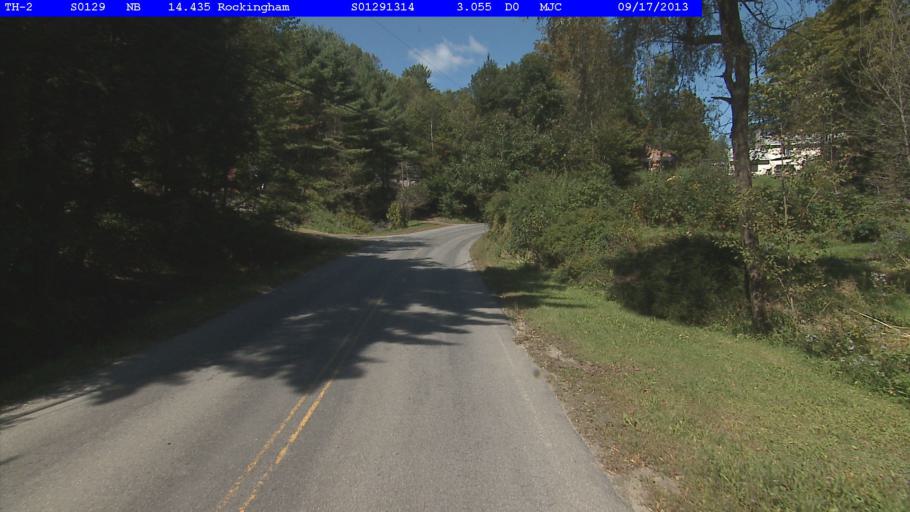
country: US
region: Vermont
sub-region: Windham County
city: Rockingham
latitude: 43.1613
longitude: -72.5175
